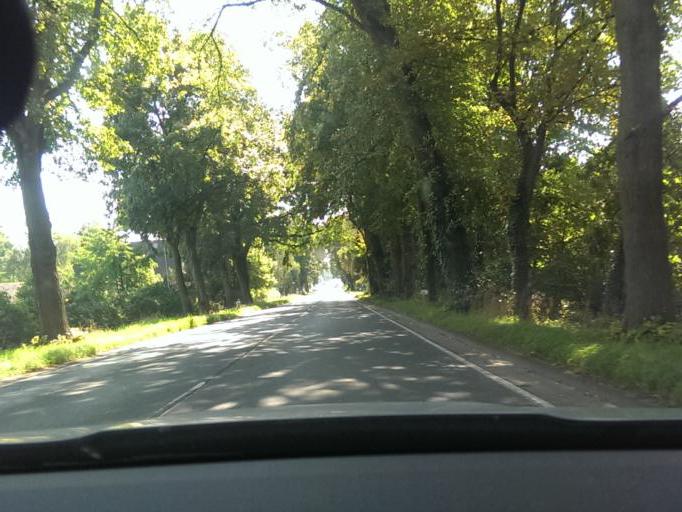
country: DE
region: Lower Saxony
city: Elze
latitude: 52.5501
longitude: 9.7243
